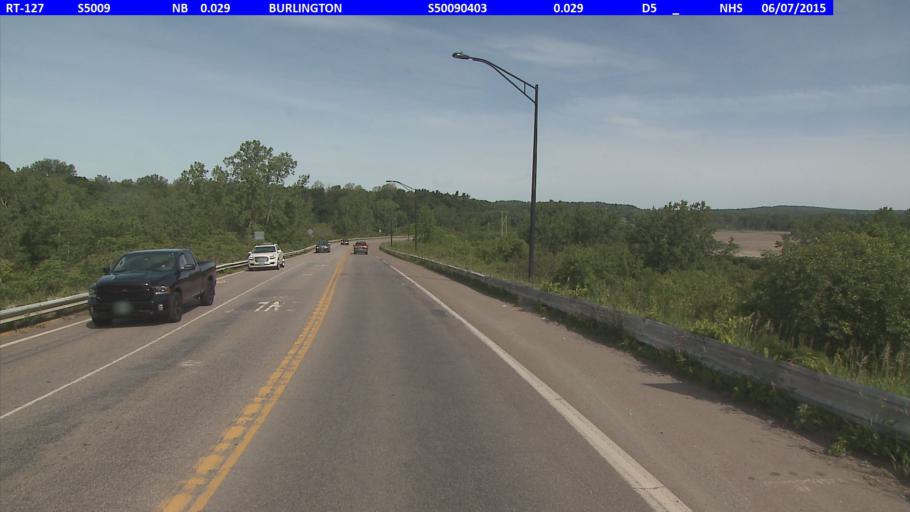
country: US
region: Vermont
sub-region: Chittenden County
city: Burlington
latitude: 44.4879
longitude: -73.2197
